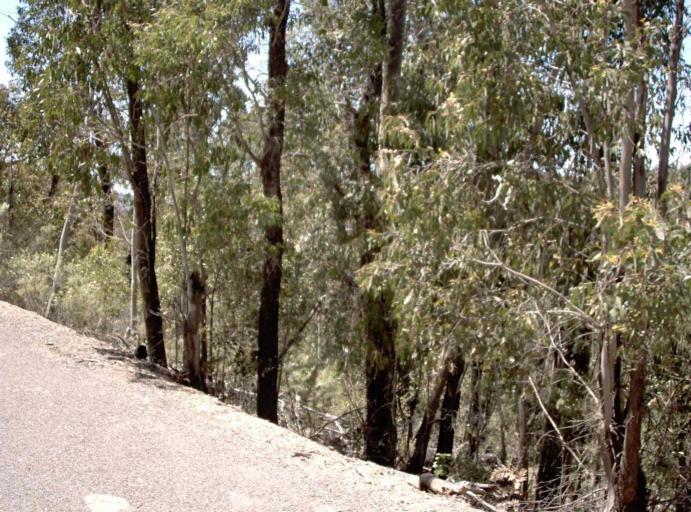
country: AU
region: New South Wales
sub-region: Snowy River
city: Jindabyne
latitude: -37.1172
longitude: 148.2441
